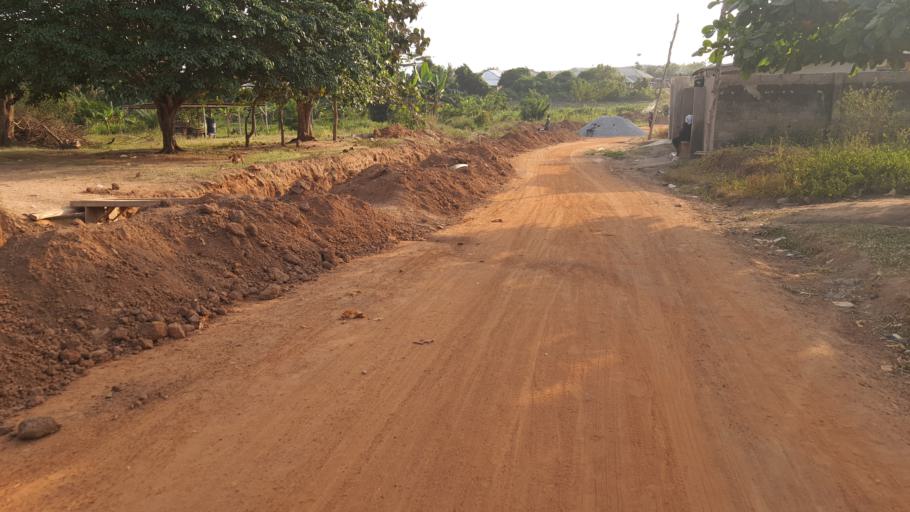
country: NG
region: Osun
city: Iwo
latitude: 7.6213
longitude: 4.1599
